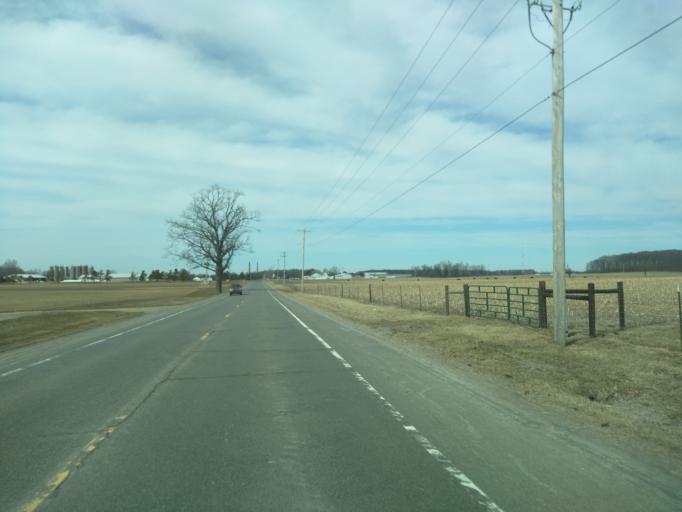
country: US
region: Michigan
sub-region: Ingham County
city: East Lansing
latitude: 42.6922
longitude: -84.4840
